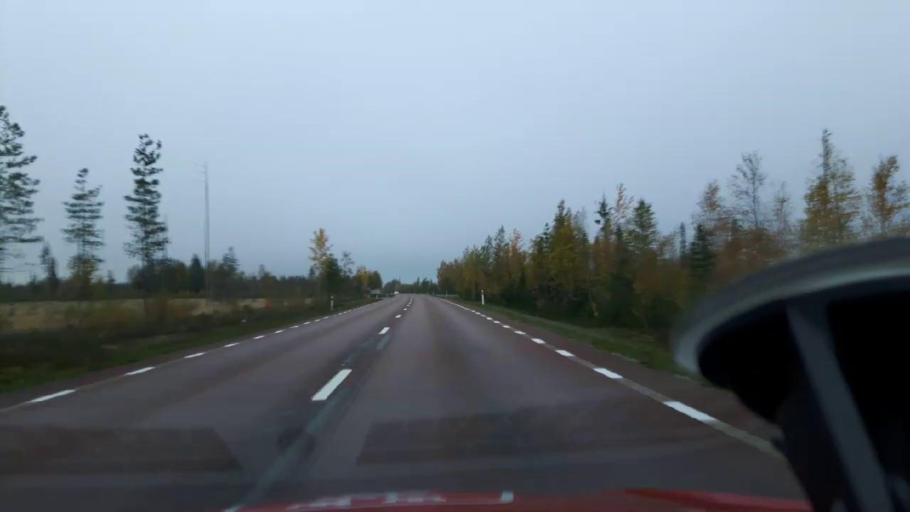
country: SE
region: Jaemtland
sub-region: Bergs Kommun
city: Hoverberg
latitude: 62.5294
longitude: 14.4469
